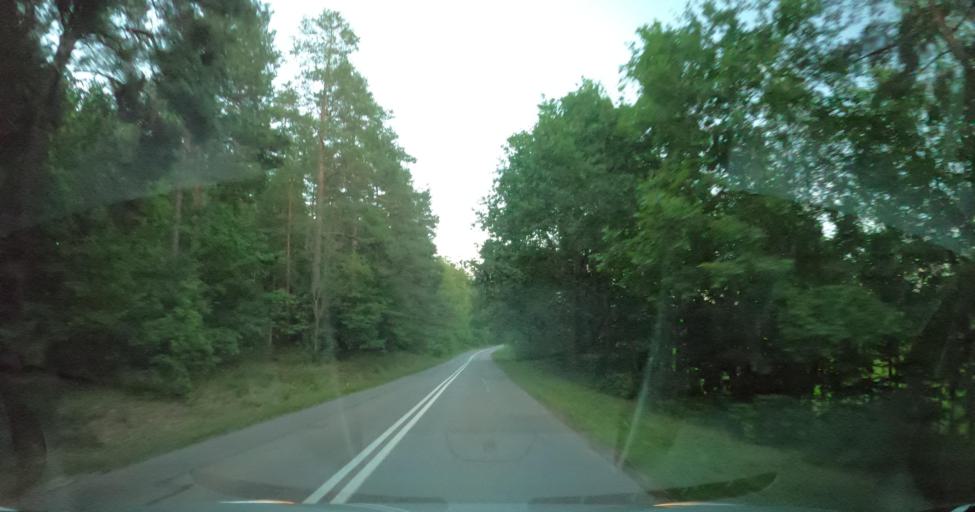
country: PL
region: Pomeranian Voivodeship
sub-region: Powiat wejherowski
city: Linia
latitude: 54.4601
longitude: 18.0010
